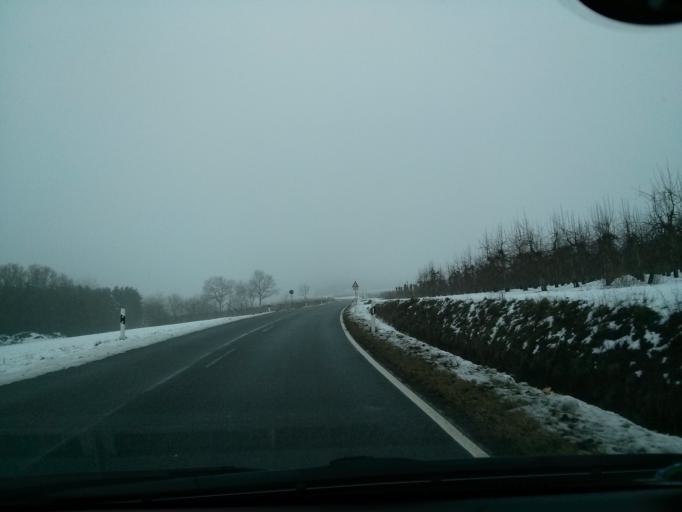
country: DE
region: Rheinland-Pfalz
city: Kalenborn
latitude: 50.5869
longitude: 7.0070
